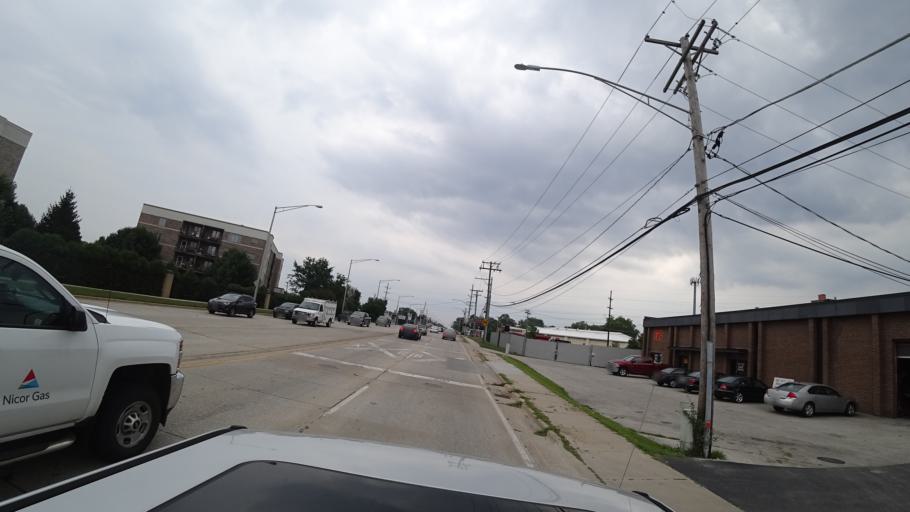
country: US
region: Illinois
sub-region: Cook County
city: Oak Lawn
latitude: 41.6968
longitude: -87.7596
